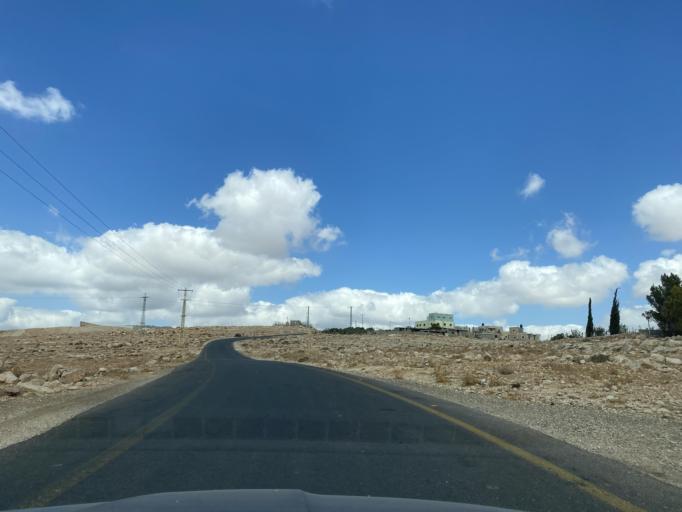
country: PS
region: West Bank
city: Marah Rabbah
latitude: 31.6143
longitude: 35.2239
